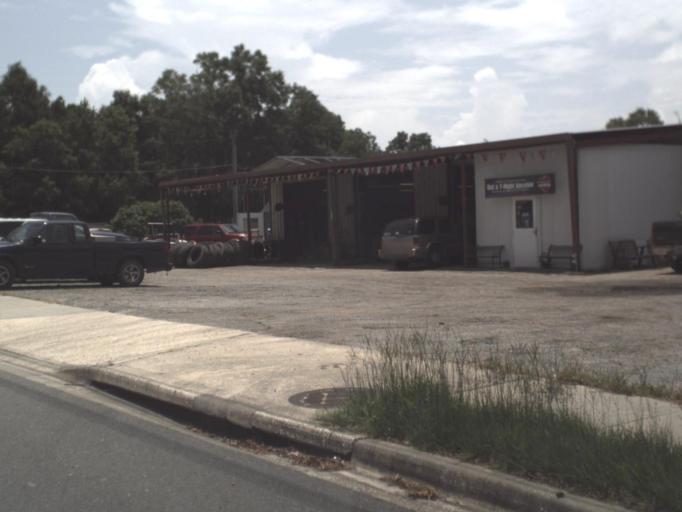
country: US
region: Florida
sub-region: Madison County
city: Madison
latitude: 30.4691
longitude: -83.3991
